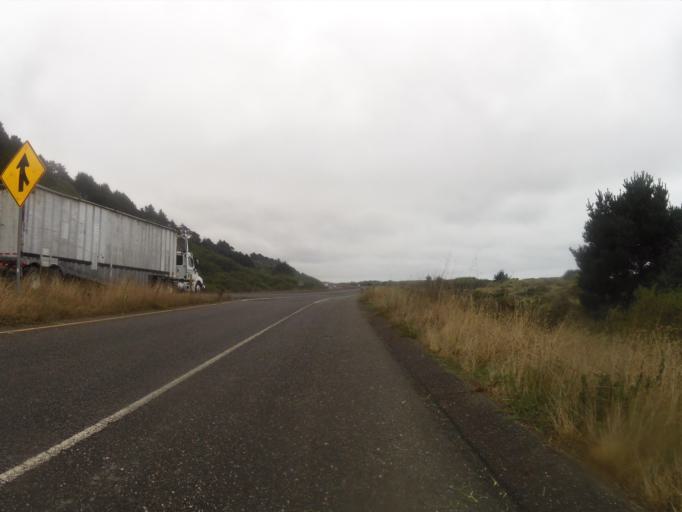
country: US
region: California
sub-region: Humboldt County
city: McKinleyville
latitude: 40.9930
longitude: -124.1142
